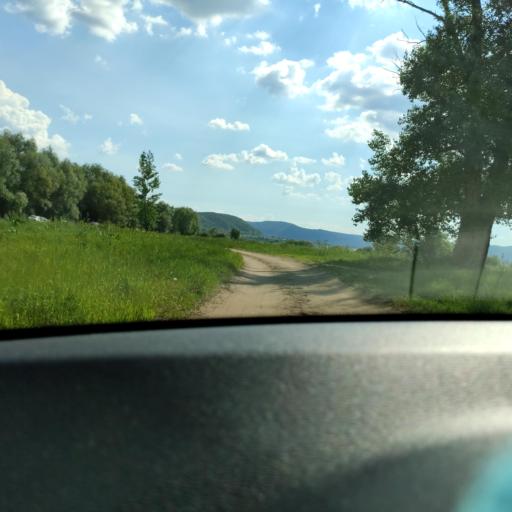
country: RU
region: Samara
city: Volzhskiy
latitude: 53.4317
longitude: 50.1658
